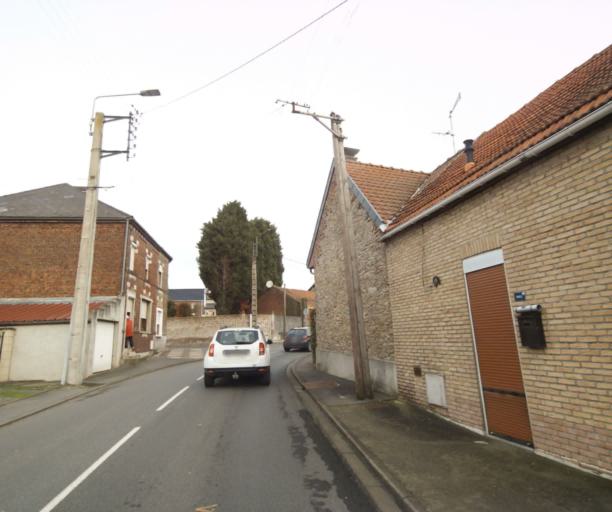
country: BE
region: Wallonia
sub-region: Province du Hainaut
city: Peruwelz
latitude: 50.4882
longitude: 3.5828
